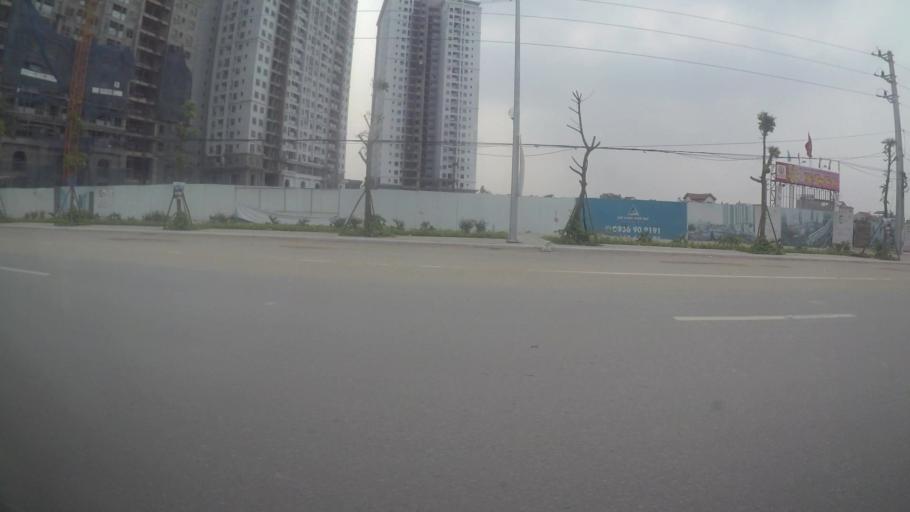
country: VN
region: Ha Noi
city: Cau Dien
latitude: 21.0485
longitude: 105.7354
